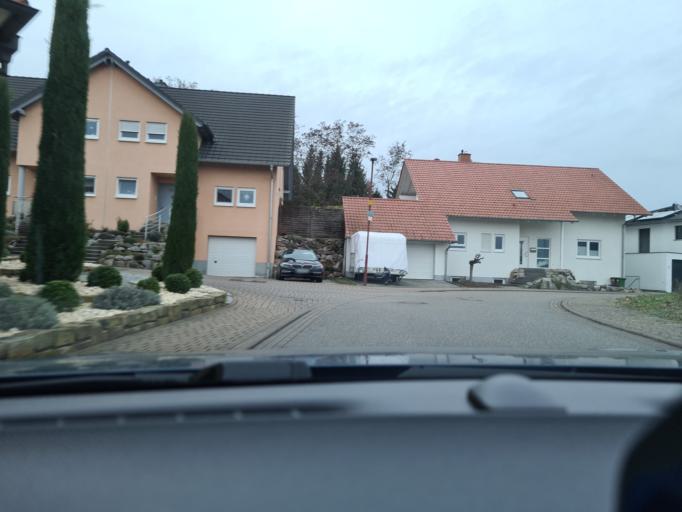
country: DE
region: Baden-Wuerttemberg
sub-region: Karlsruhe Region
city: Dielheim
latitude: 49.2867
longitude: 8.7272
